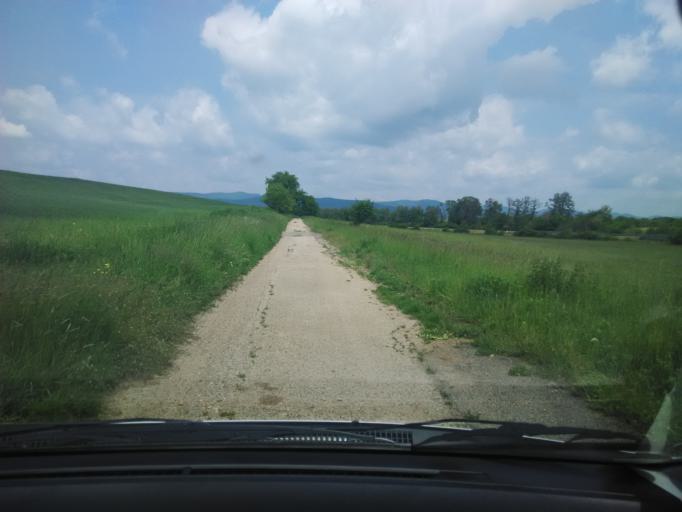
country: SK
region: Nitriansky
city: Levice
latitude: 48.2666
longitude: 18.7033
